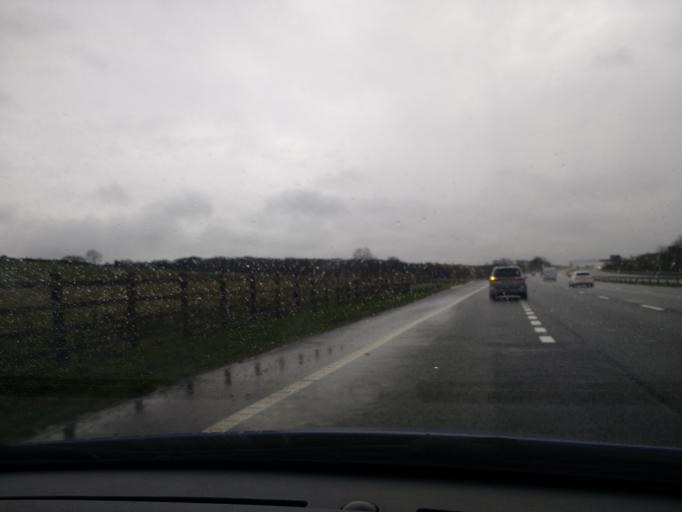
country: GB
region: England
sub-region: Lancashire
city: Bolton le Sands
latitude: 54.0709
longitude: -2.7708
